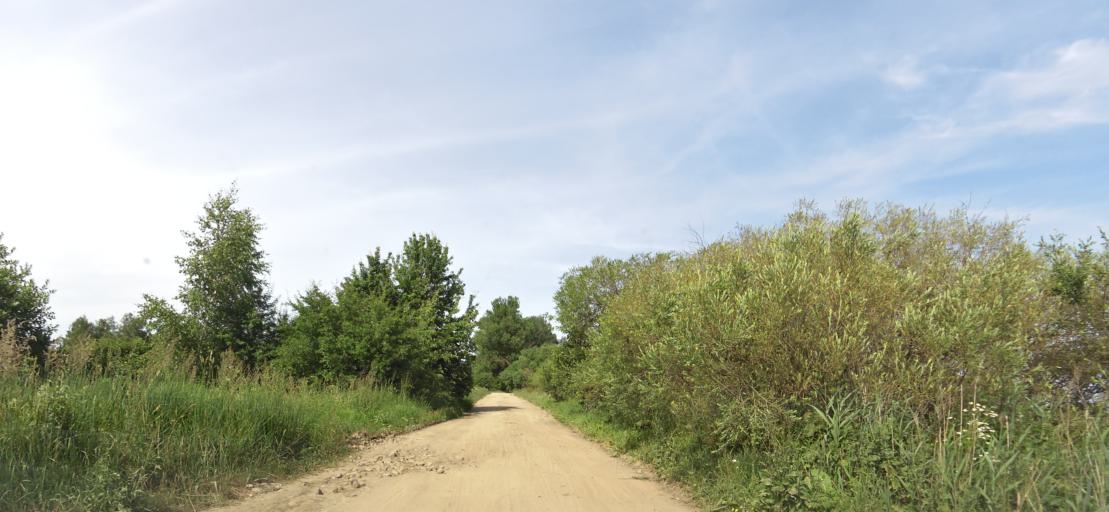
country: LT
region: Panevezys
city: Pasvalys
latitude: 55.9133
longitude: 24.2923
